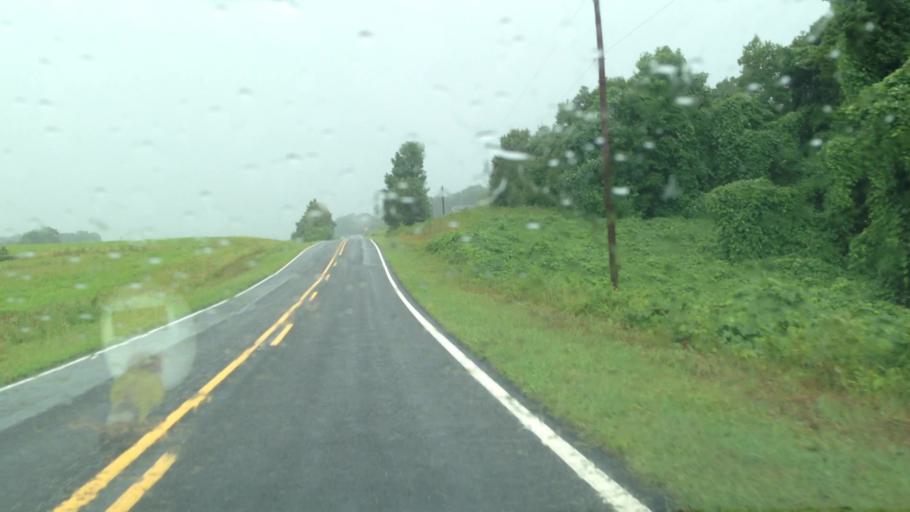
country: US
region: North Carolina
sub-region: Stokes County
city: Danbury
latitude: 36.4483
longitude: -80.0997
